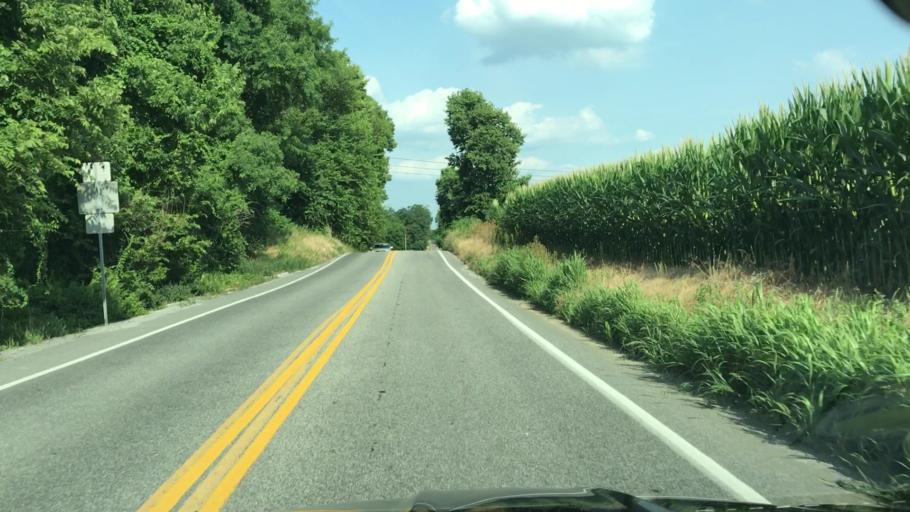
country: US
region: Pennsylvania
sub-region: Cumberland County
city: Boiling Springs
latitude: 40.1745
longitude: -77.0665
